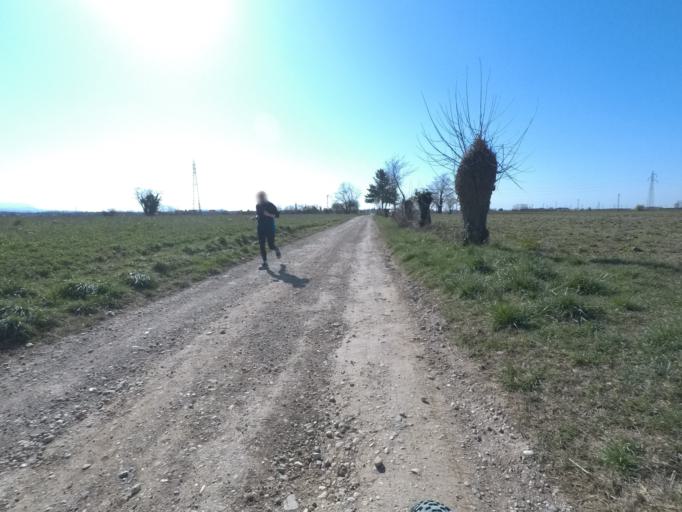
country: IT
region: Friuli Venezia Giulia
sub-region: Provincia di Udine
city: Remanzacco
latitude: 46.0965
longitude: 13.3136
